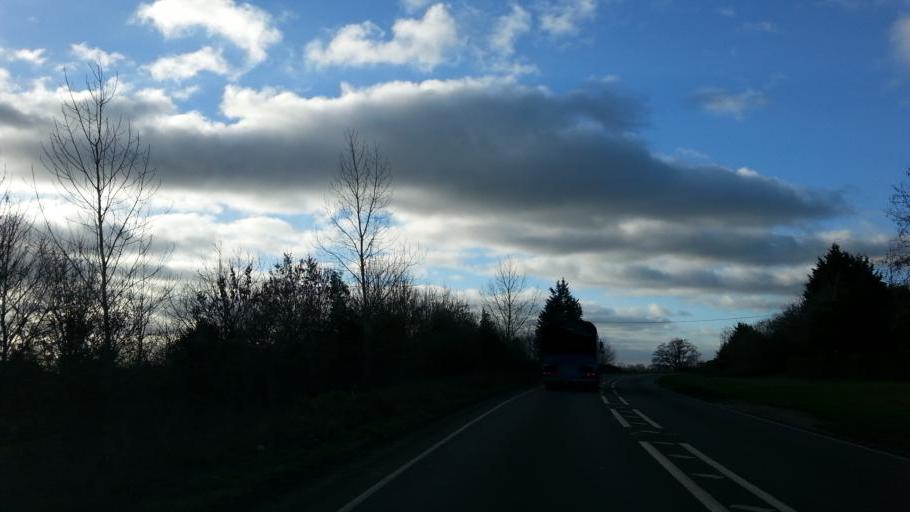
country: GB
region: England
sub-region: Norfolk
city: Harleston
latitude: 52.3642
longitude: 1.2129
